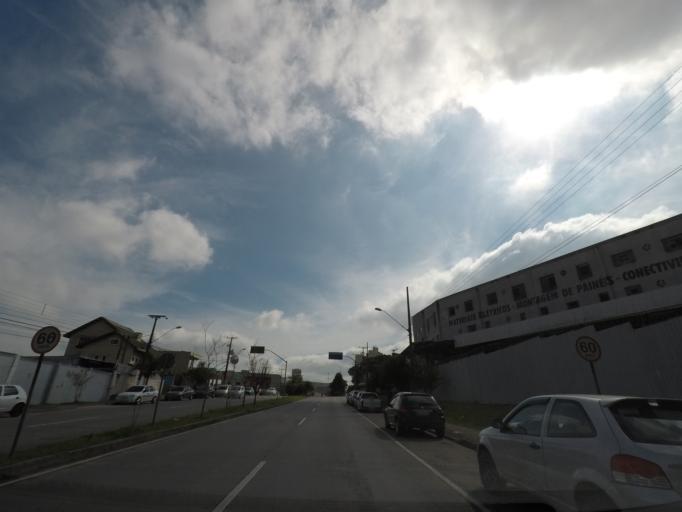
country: BR
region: Parana
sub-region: Curitiba
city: Curitiba
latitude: -25.4784
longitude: -49.2843
